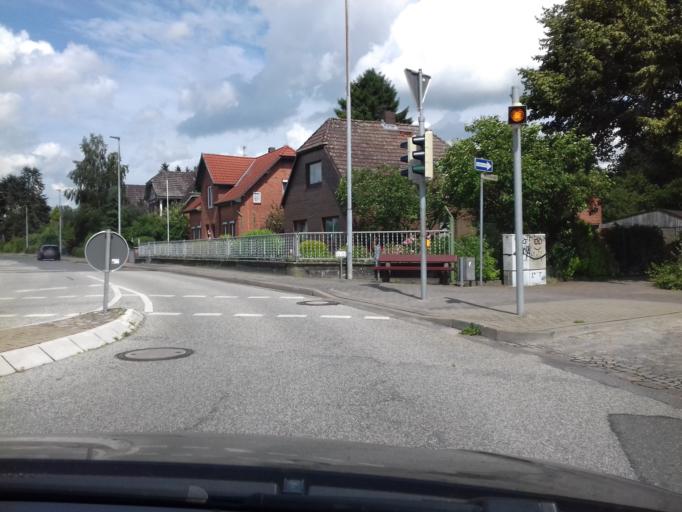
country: DE
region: Schleswig-Holstein
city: Bargteheide
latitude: 53.7349
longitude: 10.2623
